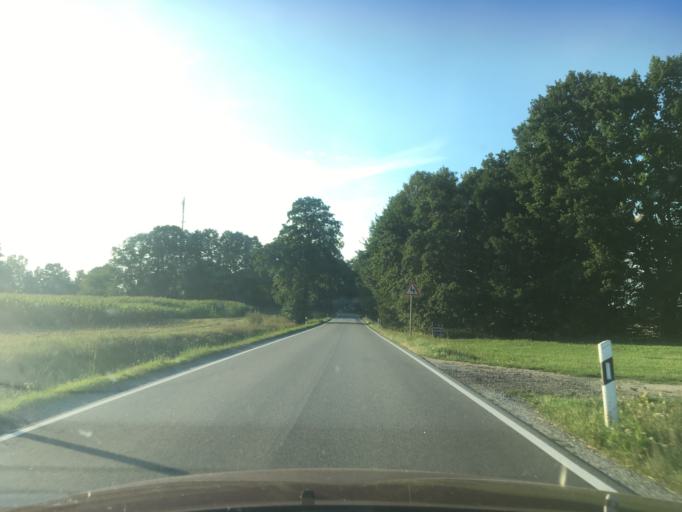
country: DE
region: Saxony
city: Rothenburg
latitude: 51.3199
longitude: 14.9803
